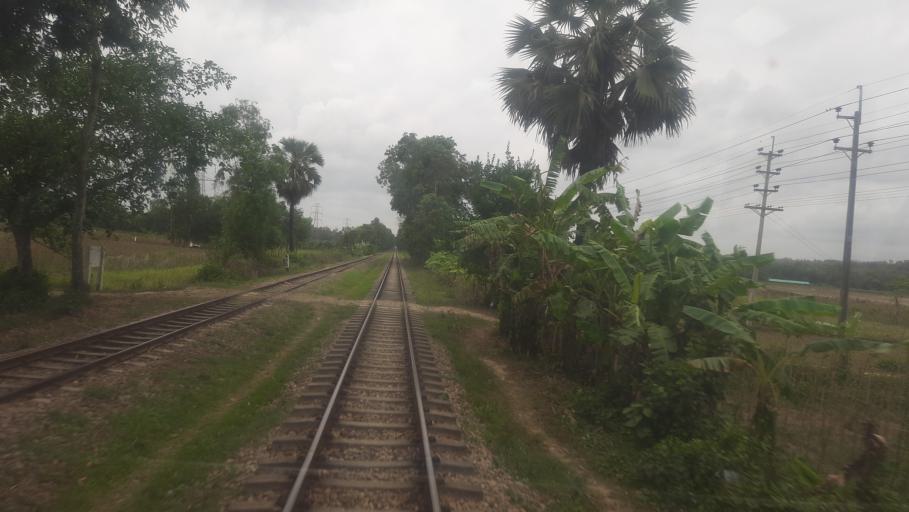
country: BD
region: Chittagong
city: Fatikchari
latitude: 22.7688
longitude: 91.5910
